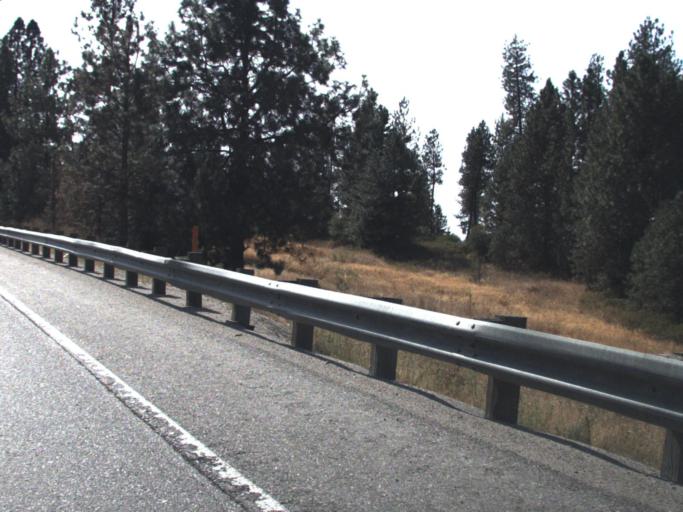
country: US
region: Washington
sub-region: Stevens County
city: Chewelah
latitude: 48.1736
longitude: -117.7042
